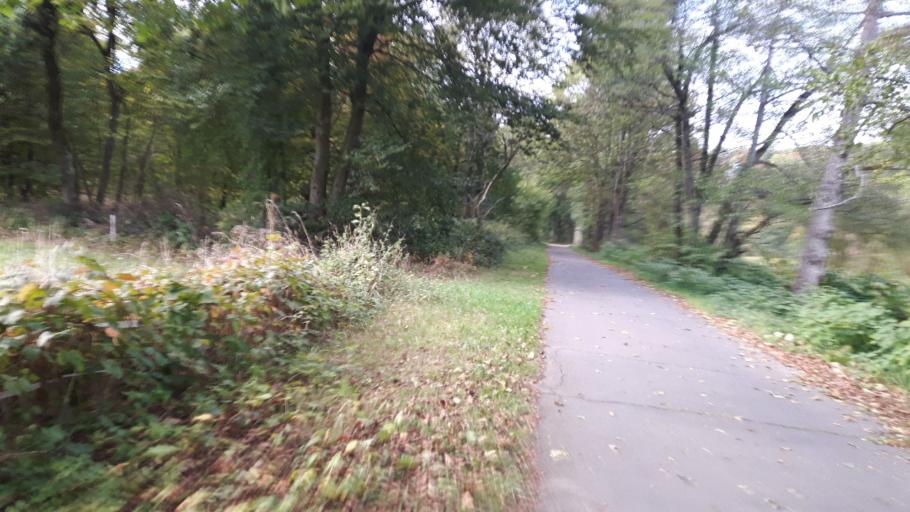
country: DE
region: Rheinland-Pfalz
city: Werkhausen
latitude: 50.7708
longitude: 7.5235
